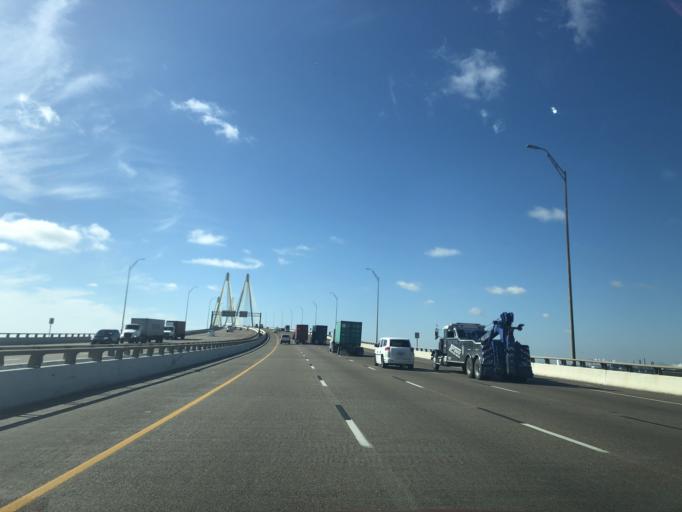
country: US
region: Texas
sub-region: Harris County
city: Baytown
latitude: 29.7100
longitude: -95.0085
